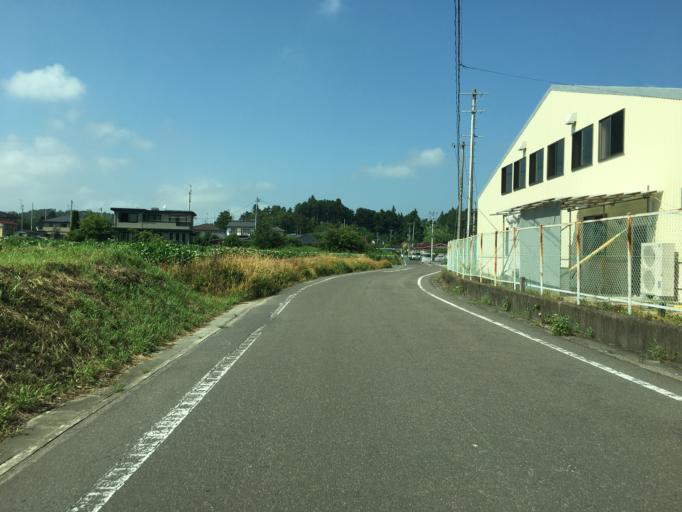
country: JP
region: Miyagi
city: Marumori
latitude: 37.8882
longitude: 140.8920
